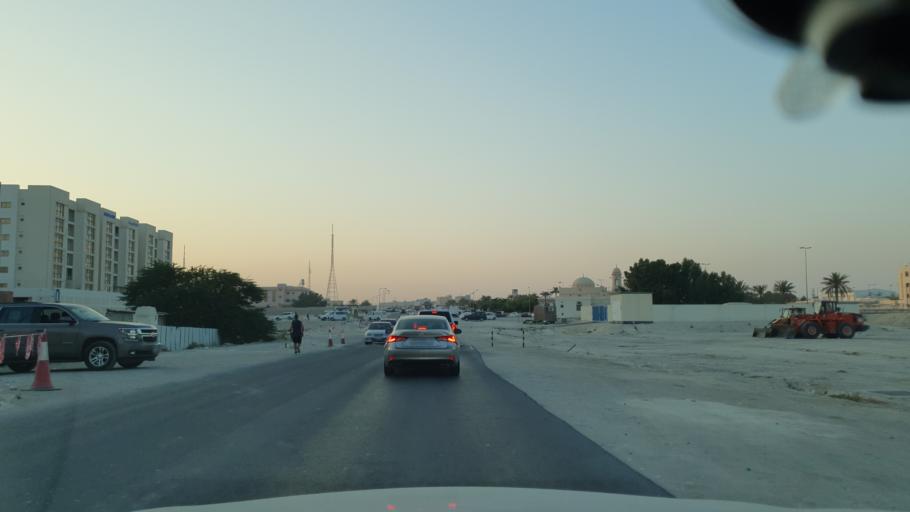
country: BH
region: Northern
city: Madinat `Isa
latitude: 26.1557
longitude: 50.5675
